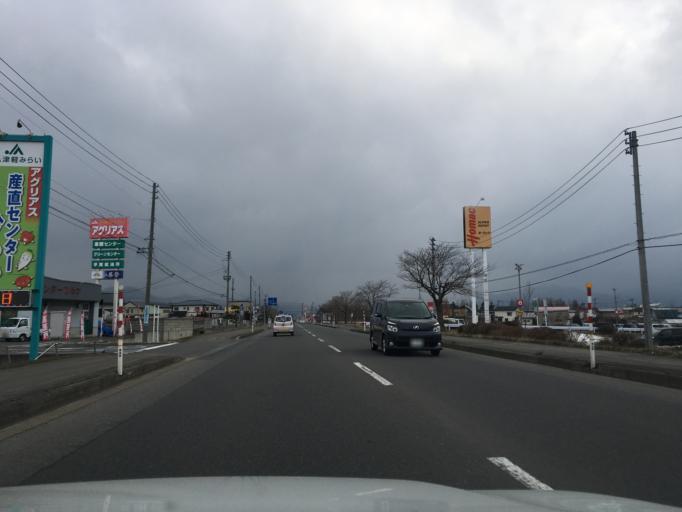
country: JP
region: Aomori
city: Kuroishi
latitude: 40.5904
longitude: 140.5691
